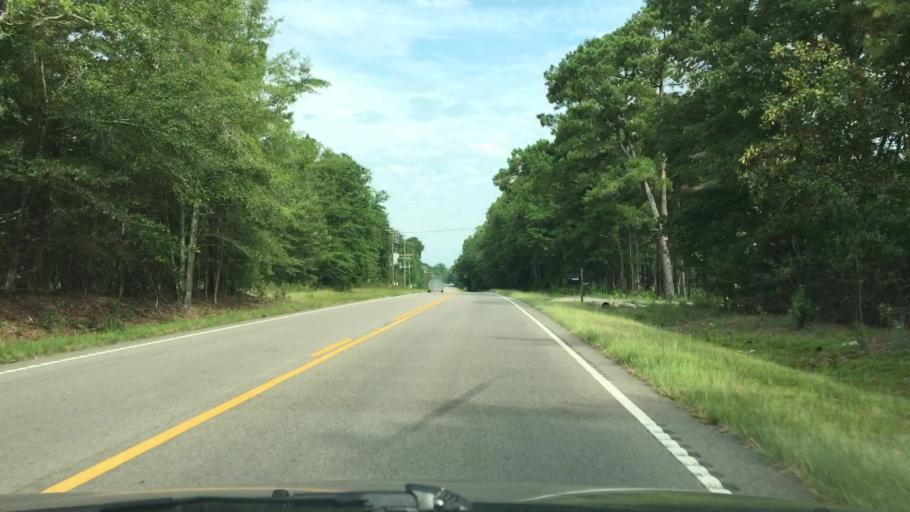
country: US
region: South Carolina
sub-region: Barnwell County
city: Williston
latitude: 33.6578
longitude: -81.3792
